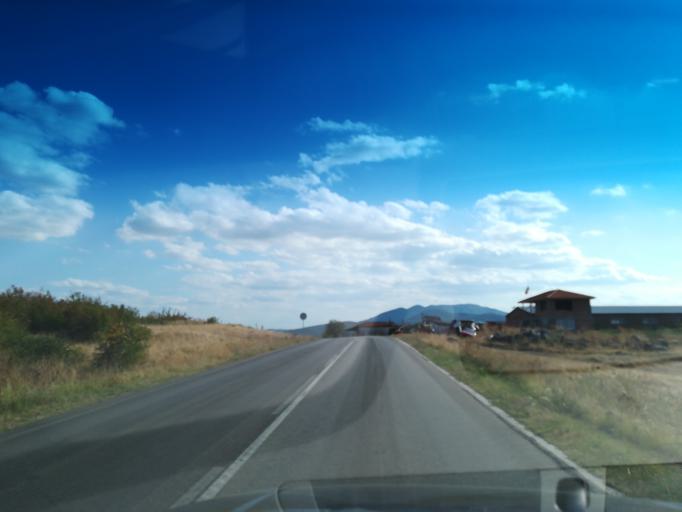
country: BG
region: Khaskovo
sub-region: Obshtina Mineralni Bani
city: Mineralni Bani
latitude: 41.9746
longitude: 25.3520
